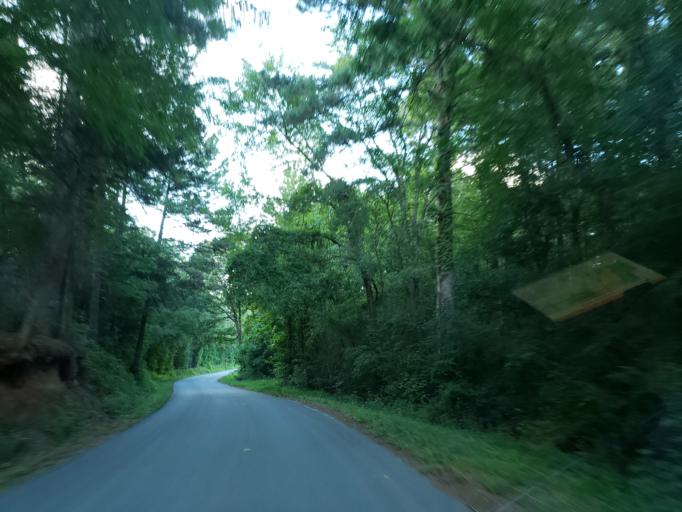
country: US
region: Georgia
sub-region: Bartow County
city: Euharlee
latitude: 34.0810
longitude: -84.9415
